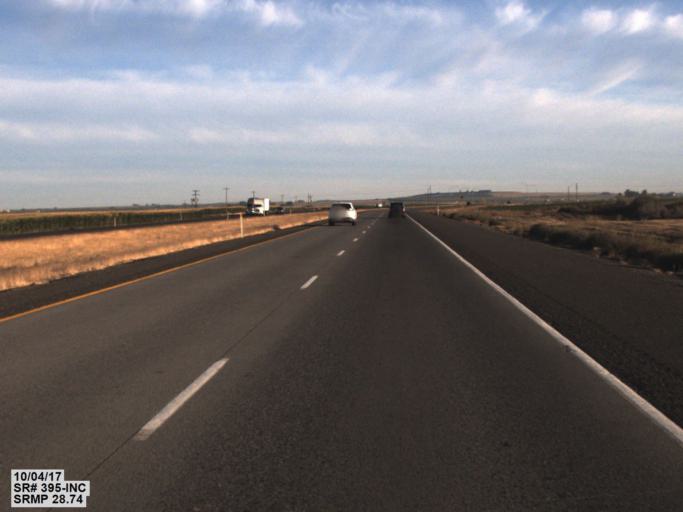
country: US
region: Washington
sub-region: Franklin County
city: Pasco
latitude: 46.3376
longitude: -119.0926
